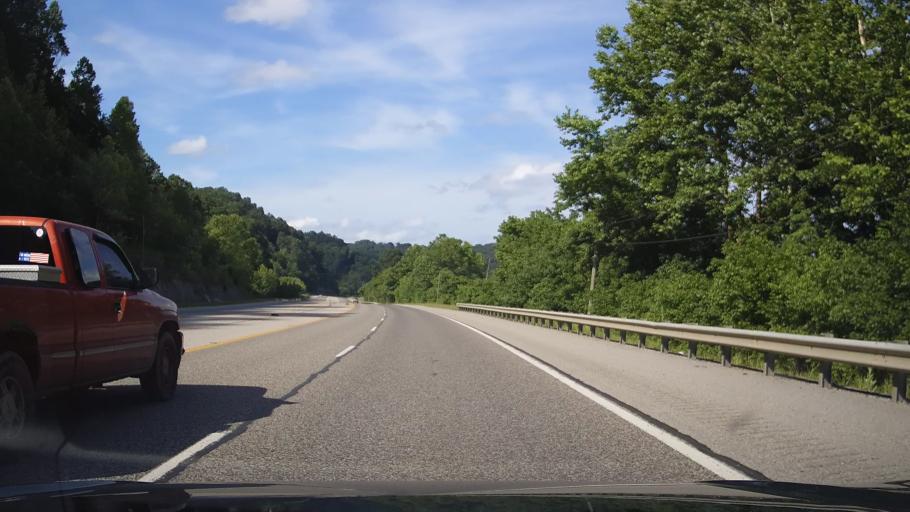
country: US
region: Kentucky
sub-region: Lawrence County
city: Louisa
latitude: 38.0122
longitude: -82.6620
